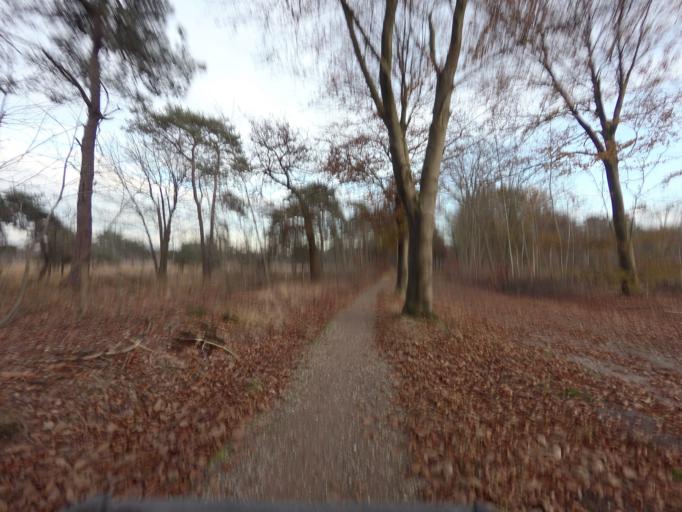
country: NL
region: North Brabant
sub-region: Gemeente Breda
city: Breda
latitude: 51.5090
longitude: 4.8087
